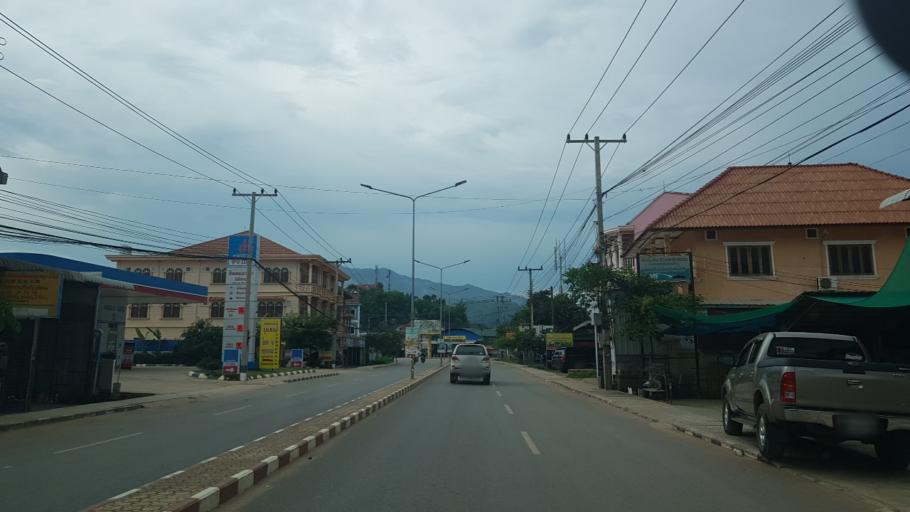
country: LA
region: Oudomxai
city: Muang Xay
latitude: 20.6841
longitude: 101.9873
